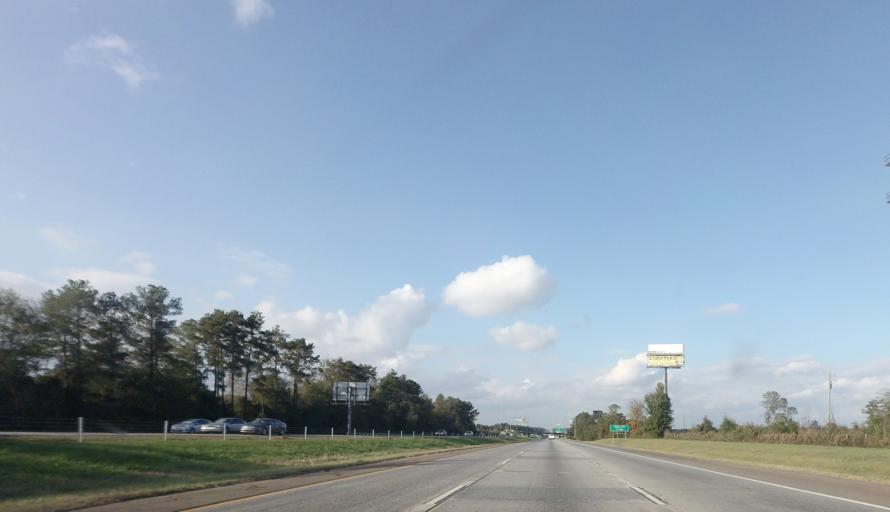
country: US
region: Georgia
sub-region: Peach County
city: Byron
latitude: 32.6057
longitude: -83.7425
